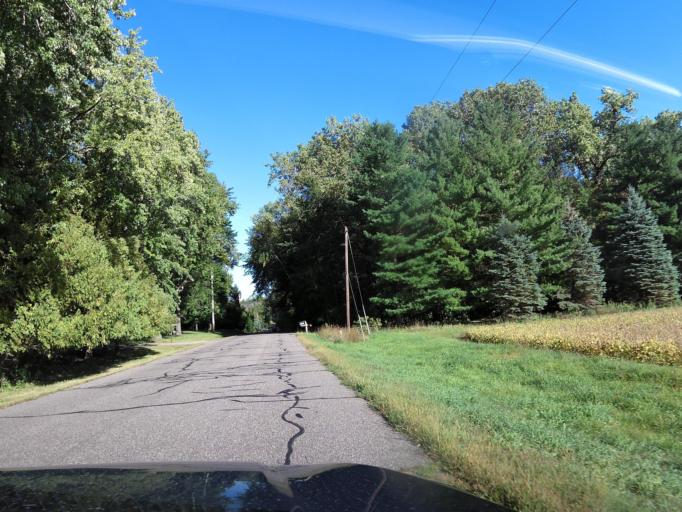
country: US
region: Minnesota
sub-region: Washington County
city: Afton
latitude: 44.8764
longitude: -92.8268
